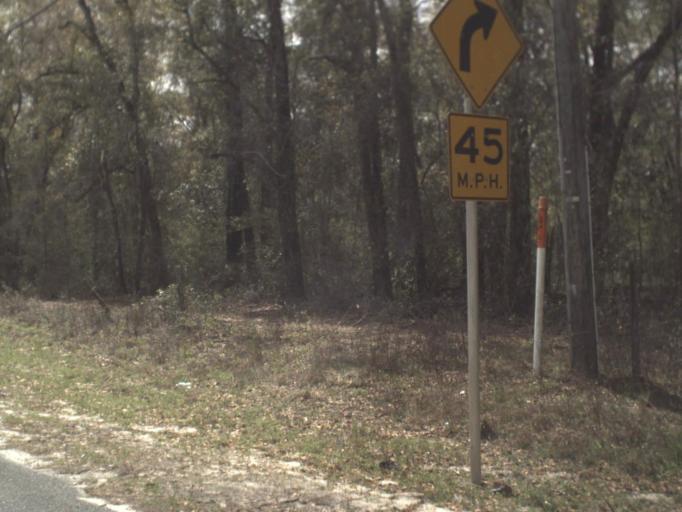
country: US
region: Florida
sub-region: Wakulla County
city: Crawfordville
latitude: 30.1573
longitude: -84.3818
